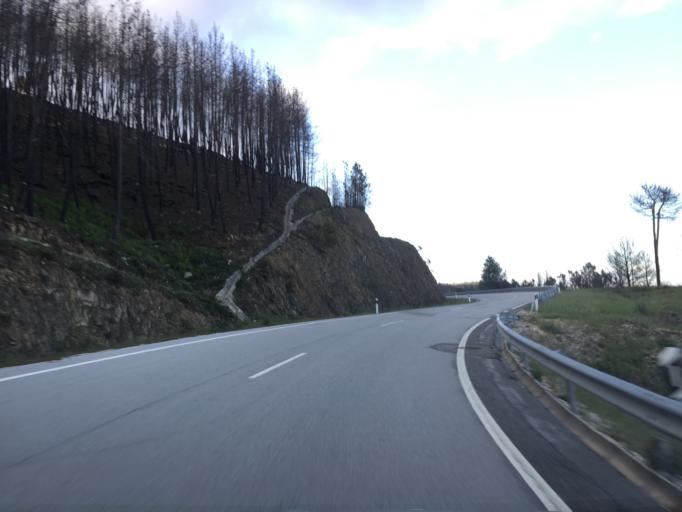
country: PT
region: Coimbra
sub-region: Gois
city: Gois
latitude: 40.0907
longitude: -8.0570
